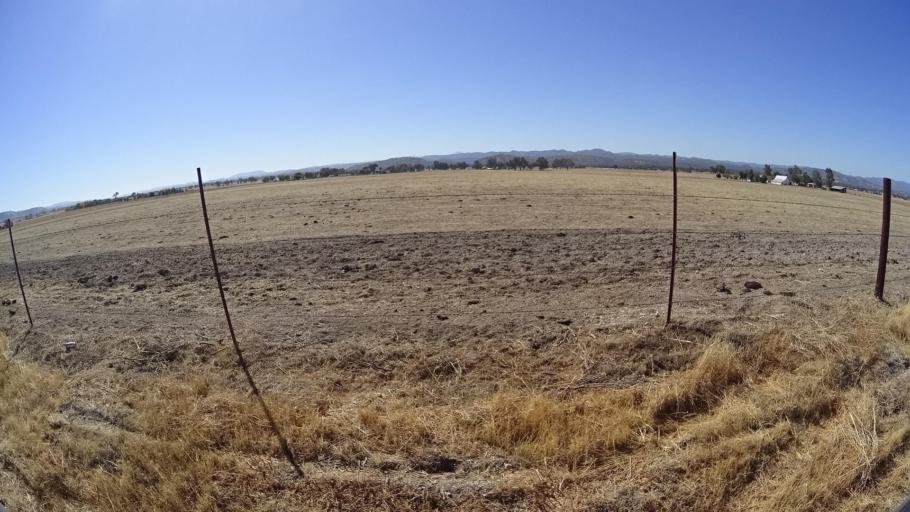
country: US
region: California
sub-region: Monterey County
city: King City
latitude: 35.9515
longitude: -121.0856
